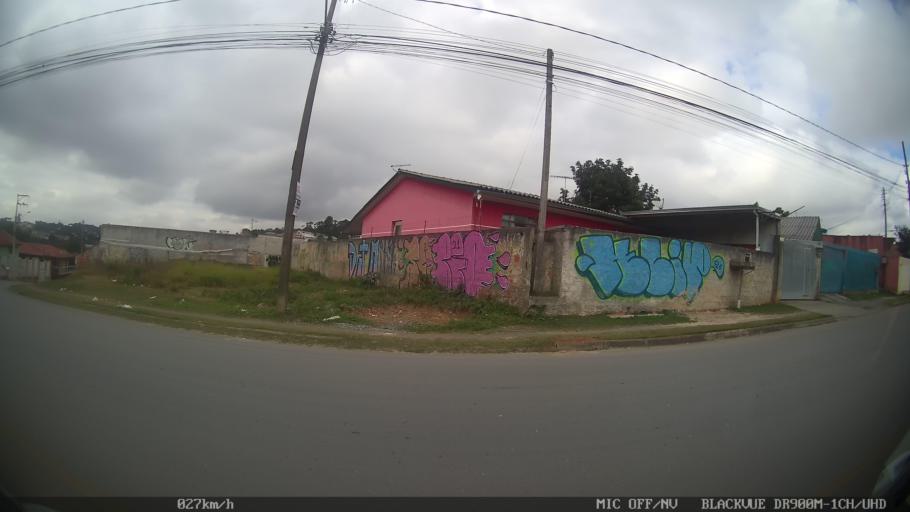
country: BR
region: Parana
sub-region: Colombo
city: Colombo
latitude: -25.3427
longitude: -49.2394
